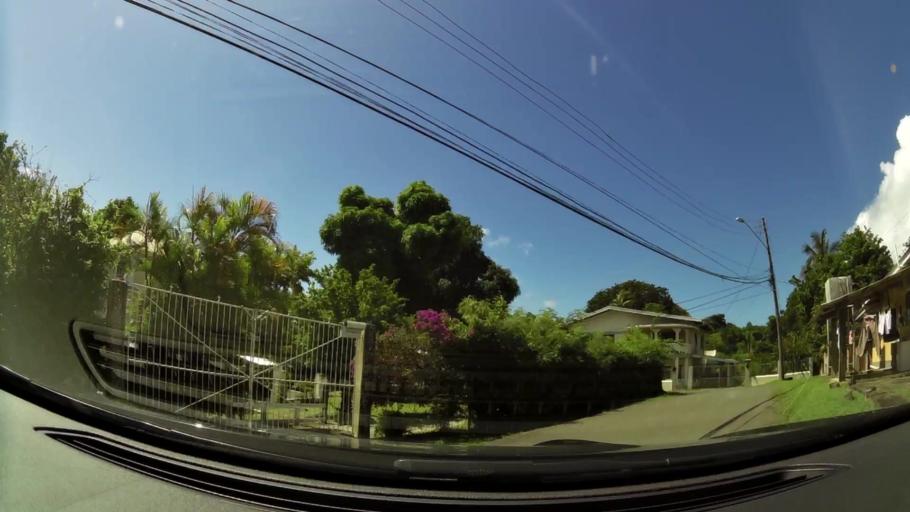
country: TT
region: Tobago
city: Scarborough
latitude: 11.1697
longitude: -60.8010
